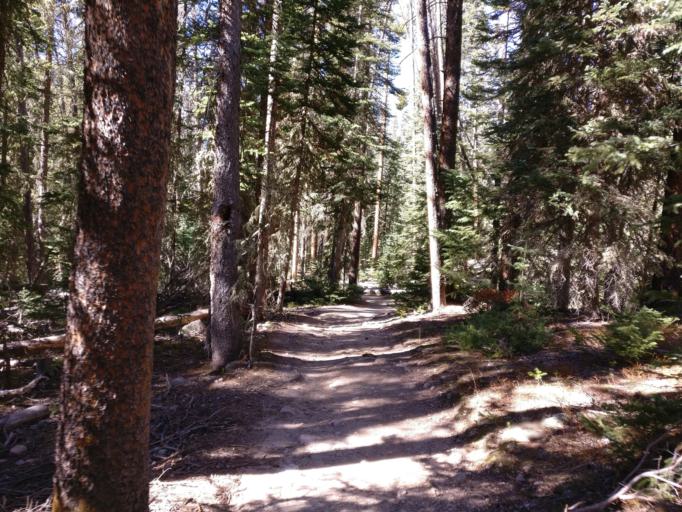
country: US
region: Colorado
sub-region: Grand County
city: Granby
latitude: 40.3100
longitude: -105.8231
